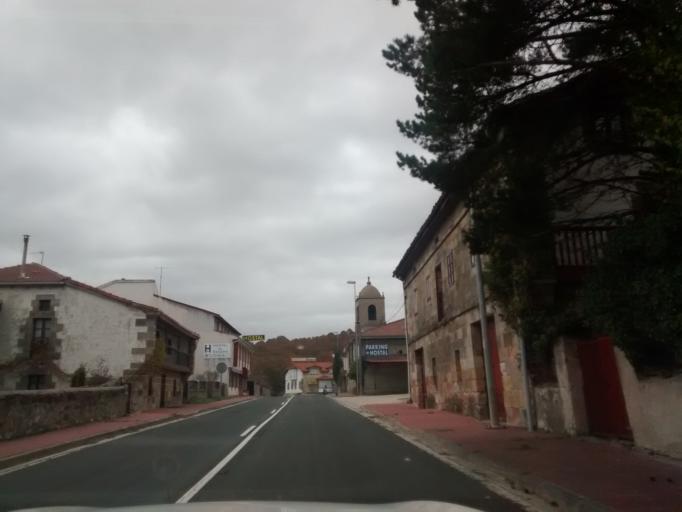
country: ES
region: Castille and Leon
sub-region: Provincia de Burgos
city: Arija
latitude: 42.9720
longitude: -3.8492
